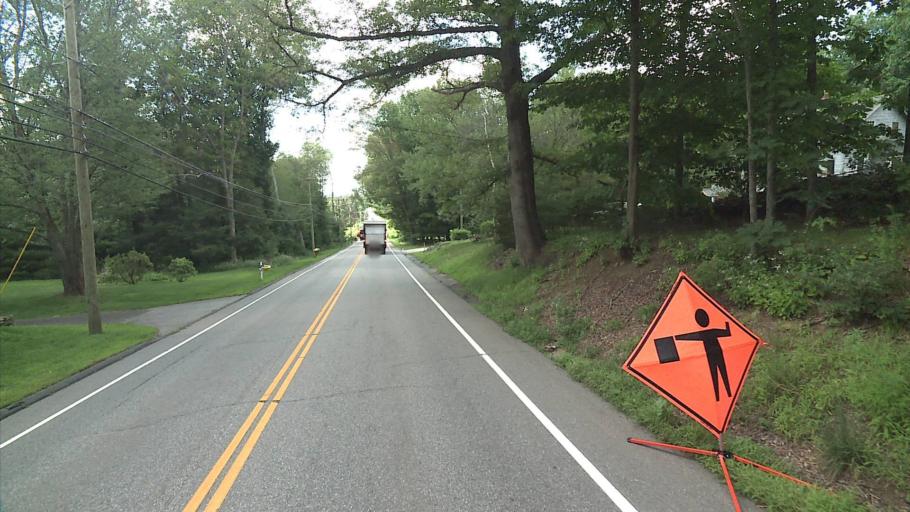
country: US
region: Connecticut
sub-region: Tolland County
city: Stafford Springs
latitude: 41.9540
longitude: -72.2757
